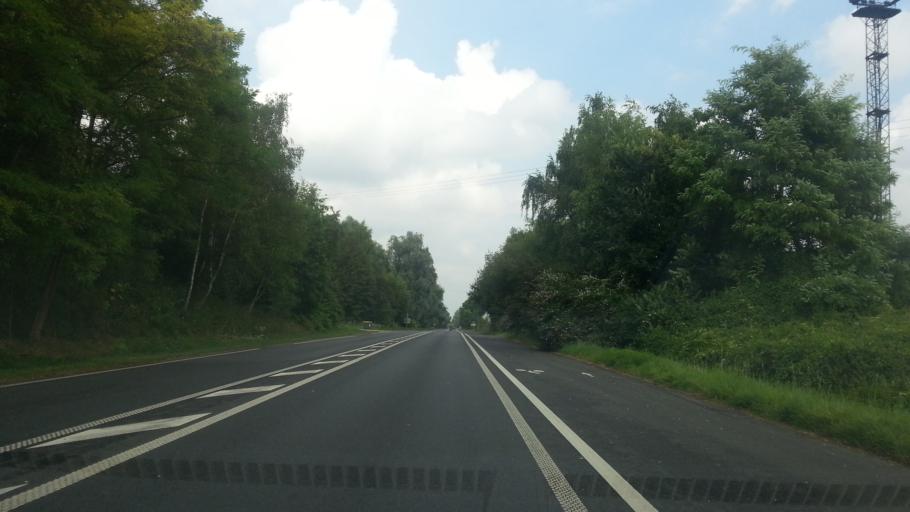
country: FR
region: Picardie
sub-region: Departement de l'Oise
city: Saint-Maximin
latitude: 49.2250
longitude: 2.4299
